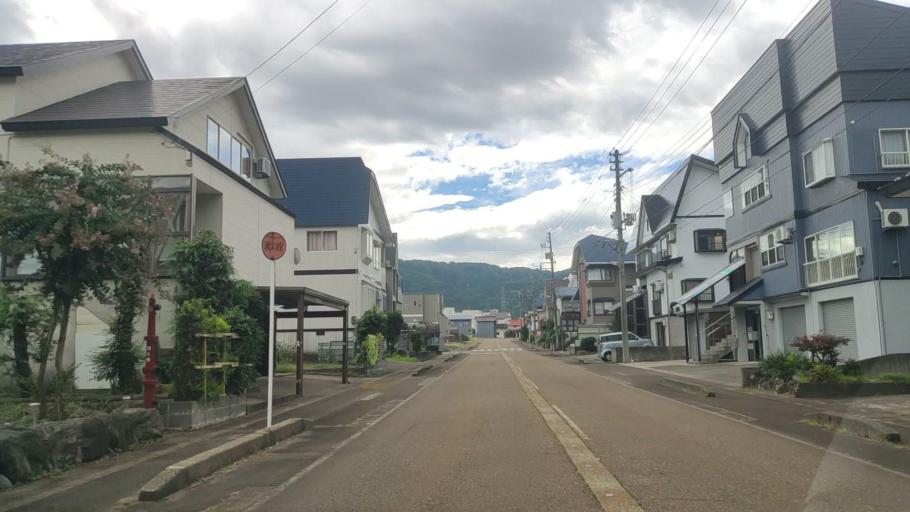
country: JP
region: Niigata
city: Arai
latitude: 37.0093
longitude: 138.2582
